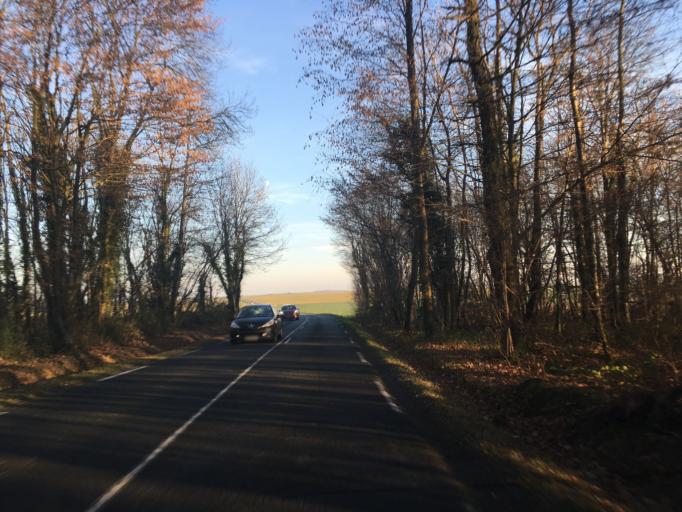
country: FR
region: Haute-Normandie
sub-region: Departement de l'Eure
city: Houlbec-Cocherel
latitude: 49.0653
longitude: 1.3866
